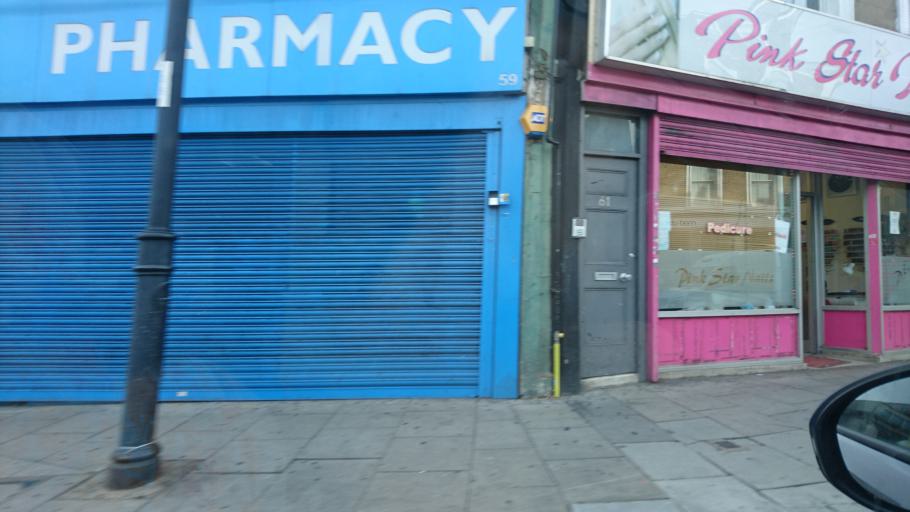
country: GB
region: England
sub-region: Greater London
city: Hackney
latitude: 51.5510
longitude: -0.0515
